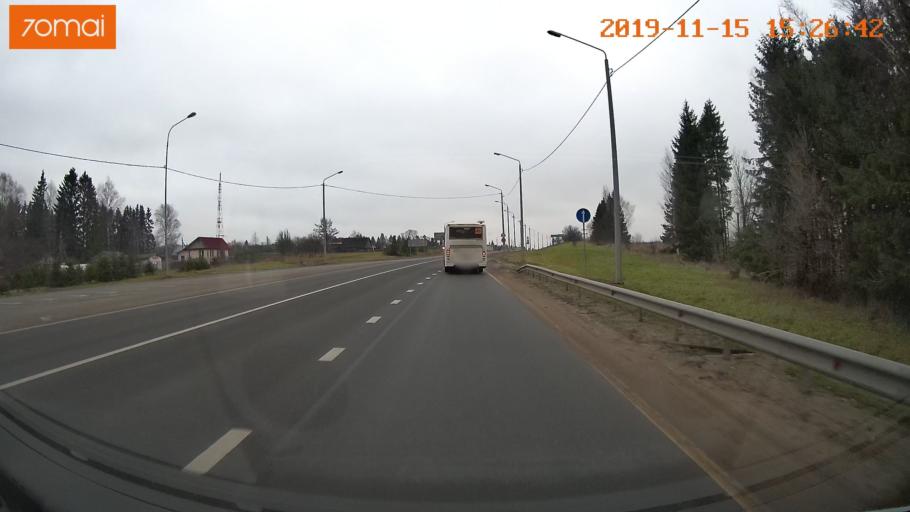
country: RU
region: Jaroslavl
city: Danilov
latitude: 58.1485
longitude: 40.1482
